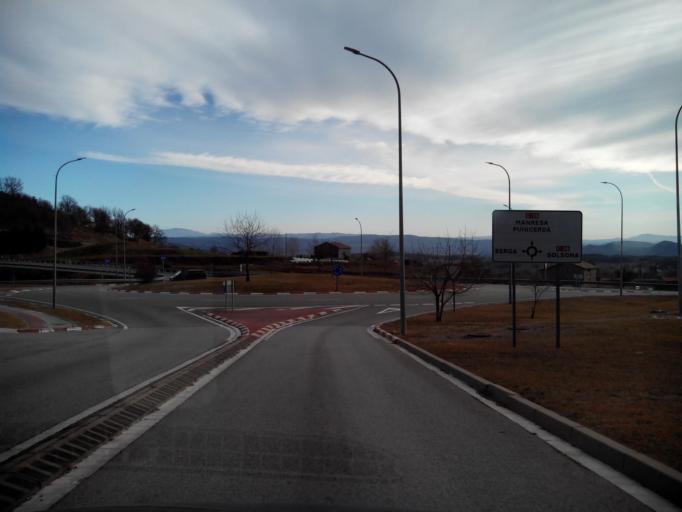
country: ES
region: Catalonia
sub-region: Provincia de Barcelona
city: Berga
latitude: 42.0898
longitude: 1.8293
